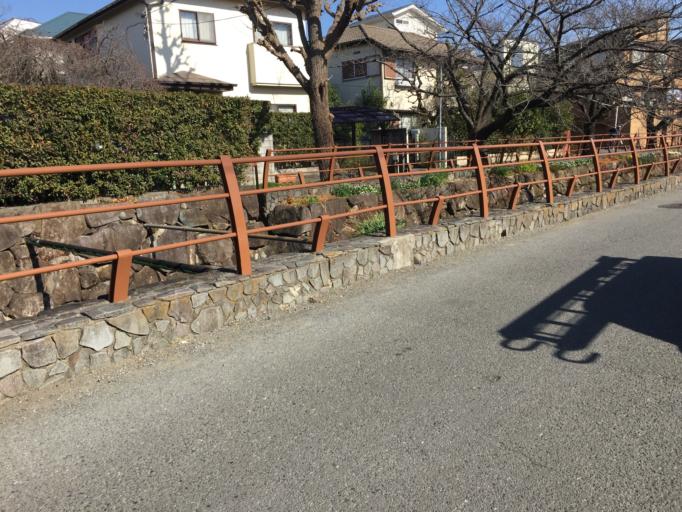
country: JP
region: Tokyo
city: Tokyo
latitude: 35.5978
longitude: 139.6554
